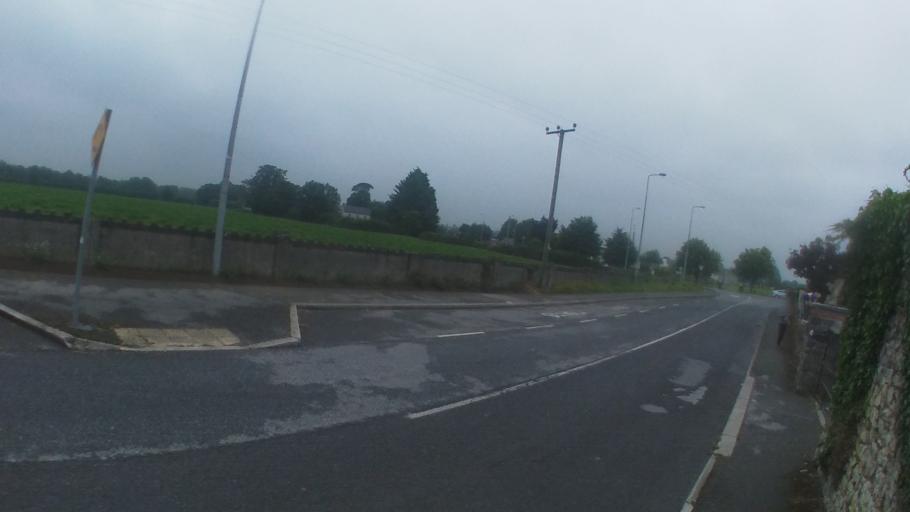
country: IE
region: Leinster
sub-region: Kilkenny
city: Callan
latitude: 52.5492
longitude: -7.3890
